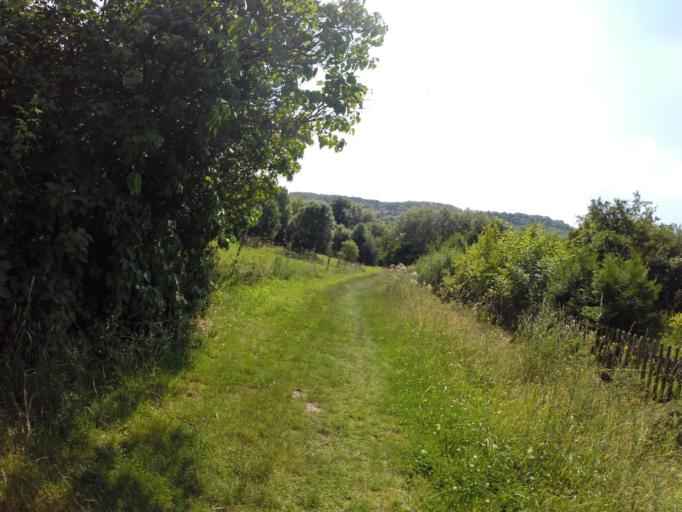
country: DE
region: Thuringia
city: Jena
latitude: 50.9294
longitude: 11.6273
